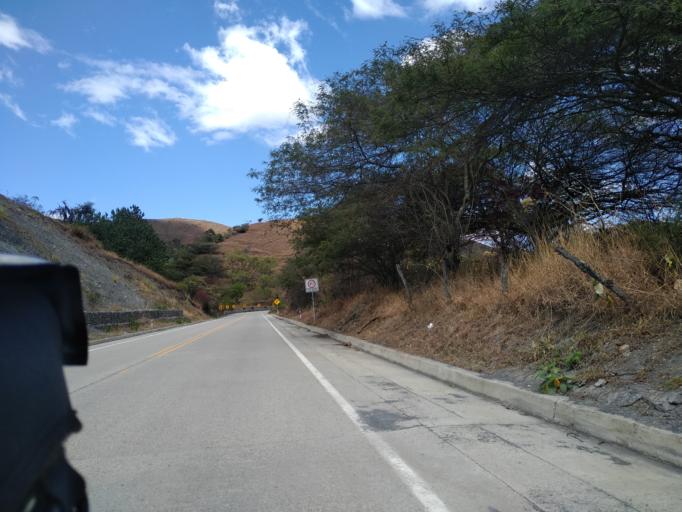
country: EC
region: Loja
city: Loja
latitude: -4.3456
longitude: -79.1886
